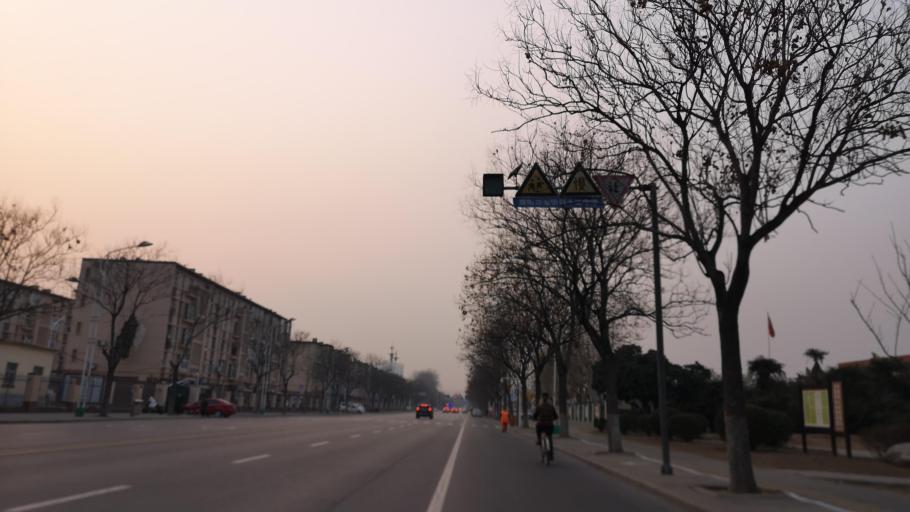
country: CN
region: Henan Sheng
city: Zhongyuanlu
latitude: 35.7844
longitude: 115.0761
